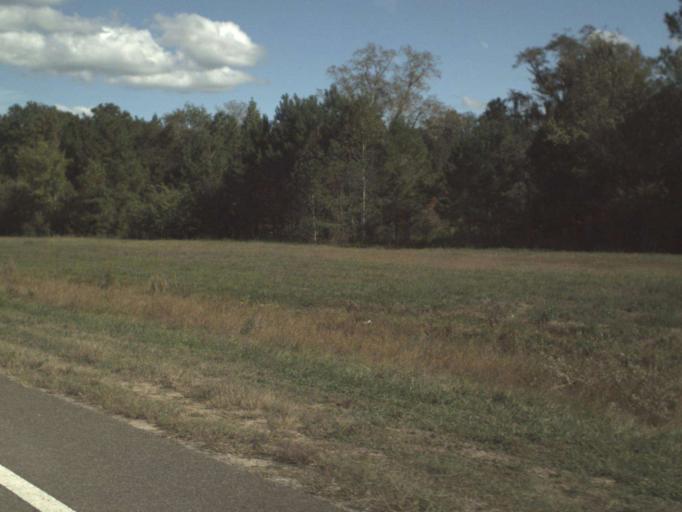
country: US
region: Florida
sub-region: Holmes County
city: Bonifay
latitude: 30.7755
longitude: -85.8077
